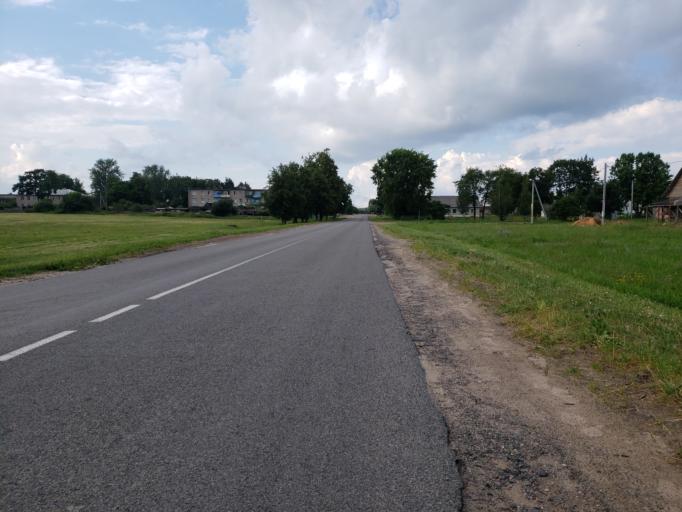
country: BY
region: Minsk
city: Chervyen'
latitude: 53.7326
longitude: 28.3882
